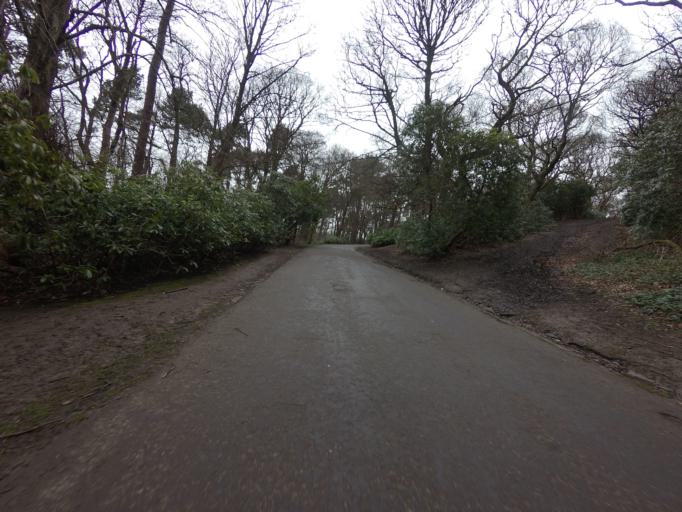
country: GB
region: Scotland
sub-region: East Renfrewshire
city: Giffnock
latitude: 55.8324
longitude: -4.3139
